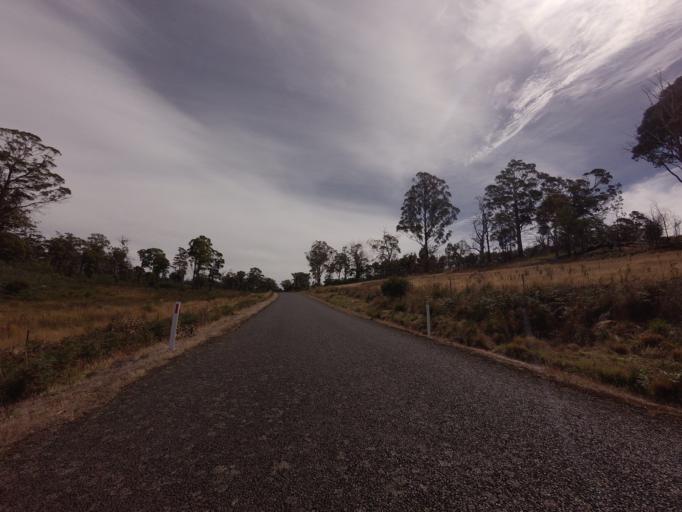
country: AU
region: Tasmania
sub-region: Sorell
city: Sorell
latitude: -42.5567
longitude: 147.6790
